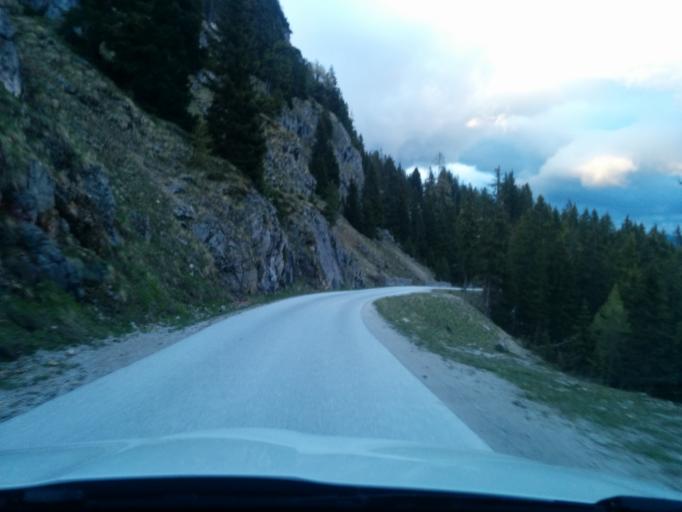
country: AT
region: Styria
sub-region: Politischer Bezirk Liezen
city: Aich
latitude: 47.4537
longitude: 13.8207
